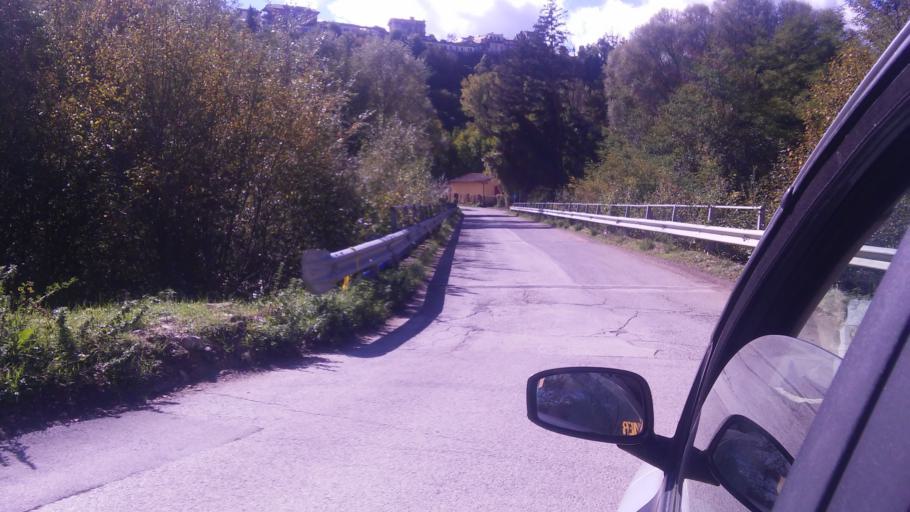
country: IT
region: Latium
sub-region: Provincia di Rieti
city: Amatrice
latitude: 42.6323
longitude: 13.2932
